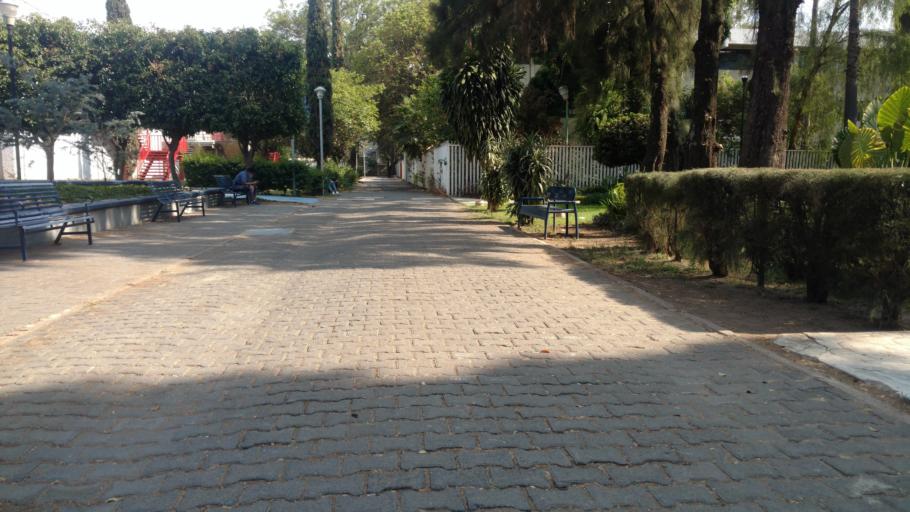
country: MX
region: Jalisco
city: Tlaquepaque
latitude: 20.6573
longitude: -103.3265
